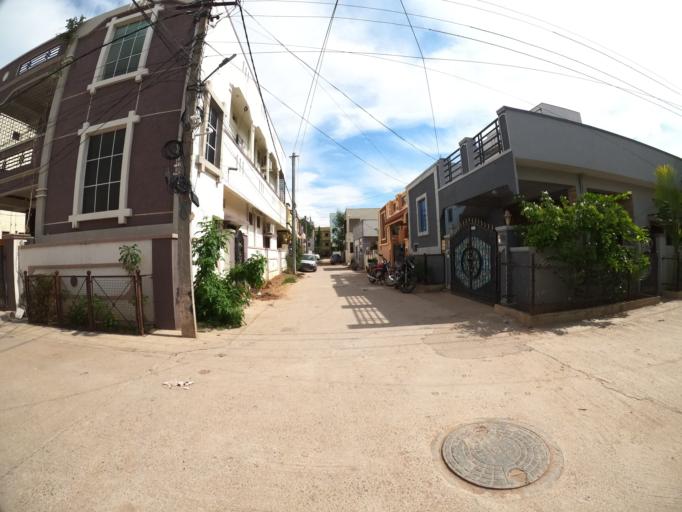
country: IN
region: Telangana
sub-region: Hyderabad
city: Hyderabad
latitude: 17.3657
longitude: 78.3866
